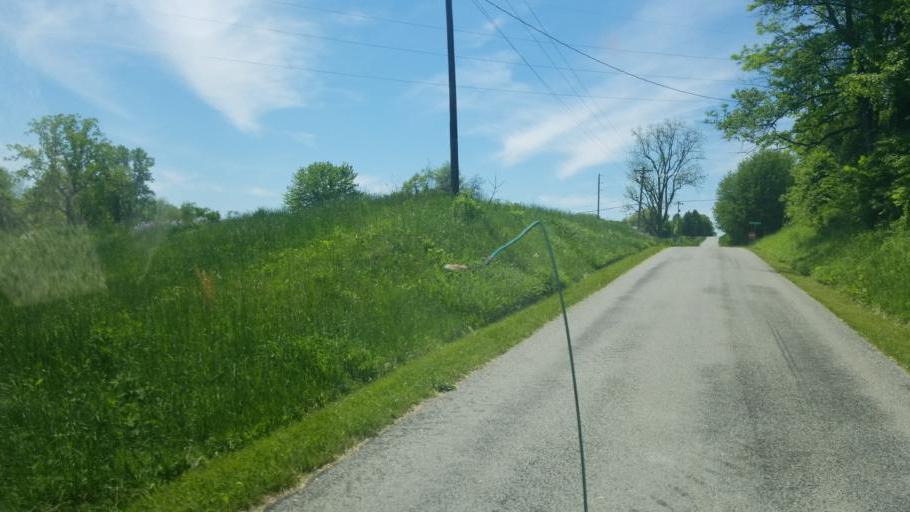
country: US
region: Ohio
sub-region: Huron County
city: Willard
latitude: 41.1200
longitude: -82.6847
